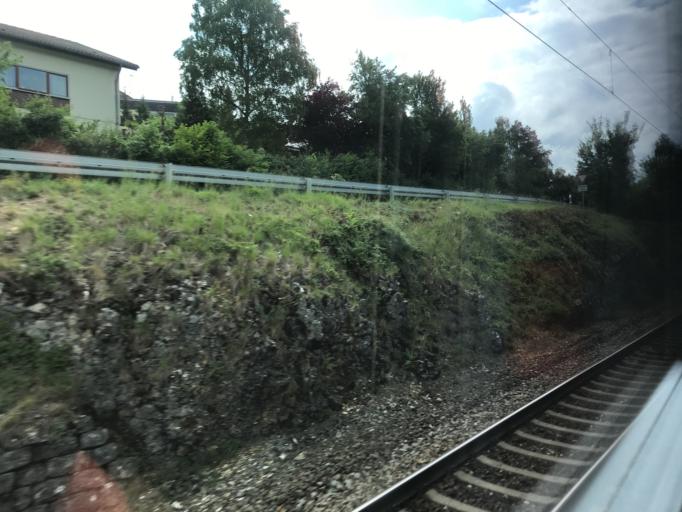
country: DE
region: Baden-Wuerttemberg
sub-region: Tuebingen Region
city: Lonsee
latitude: 48.5409
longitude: 9.9214
